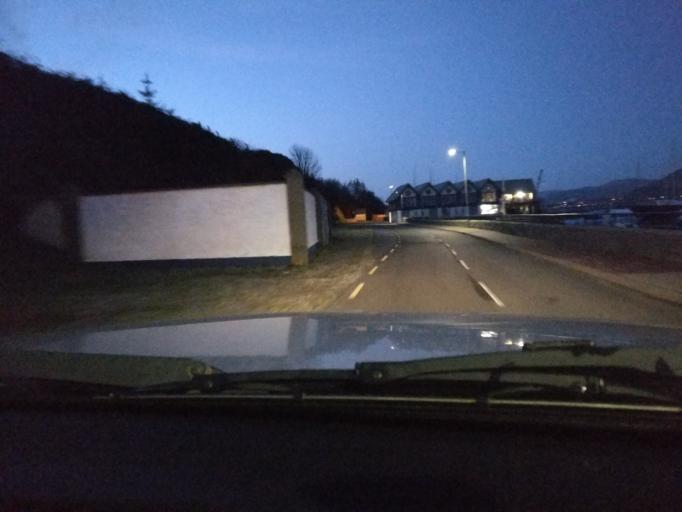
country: IE
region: Leinster
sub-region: Lu
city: Carlingford
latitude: 54.0504
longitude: -6.1919
